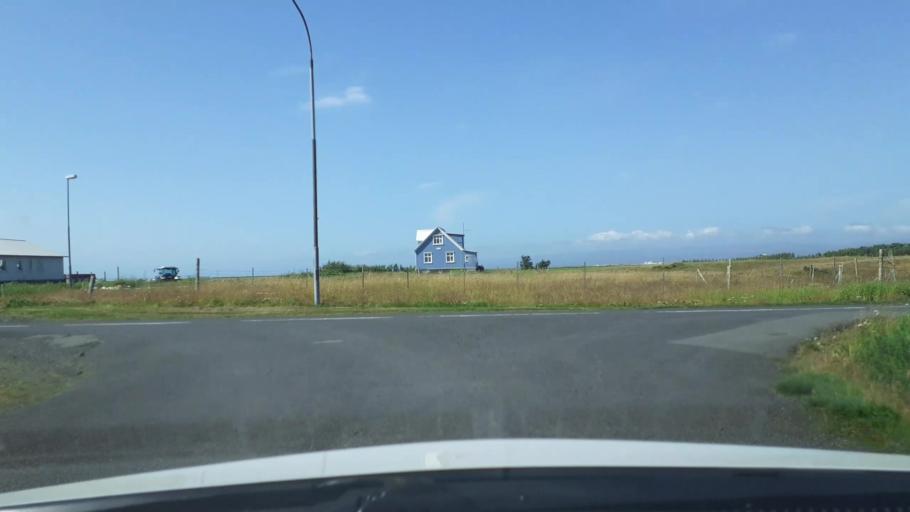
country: IS
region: South
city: Selfoss
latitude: 63.8415
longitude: -21.0523
